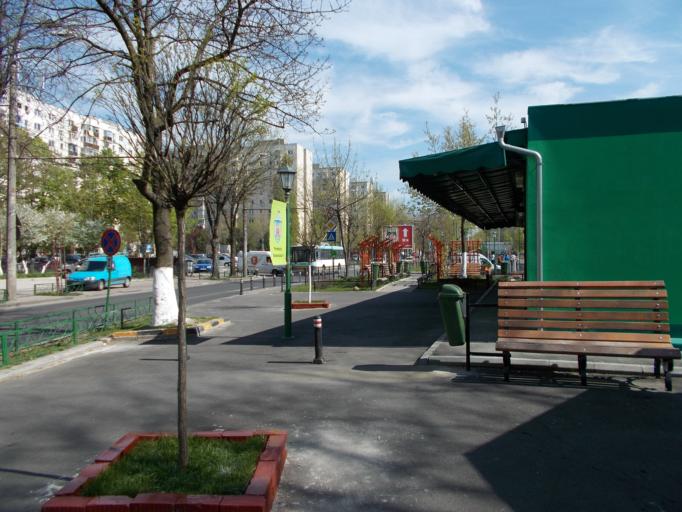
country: RO
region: Bucuresti
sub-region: Municipiul Bucuresti
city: Bucuresti
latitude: 44.3822
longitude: 26.0997
